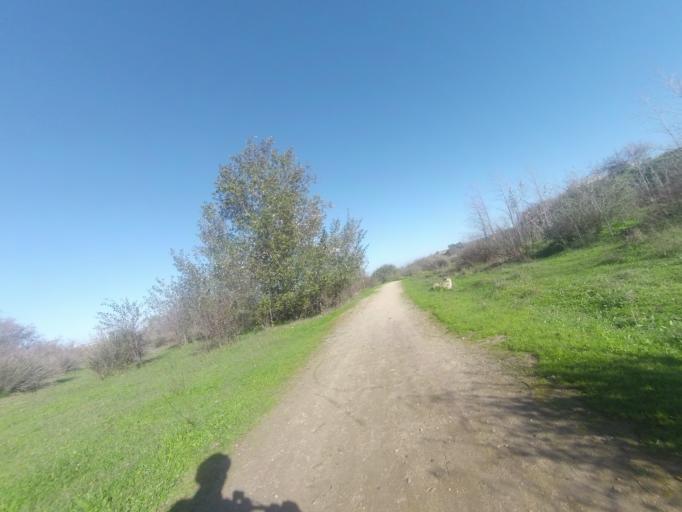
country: ES
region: Andalusia
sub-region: Provincia de Huelva
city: Palos de la Frontera
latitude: 37.2344
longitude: -6.8959
